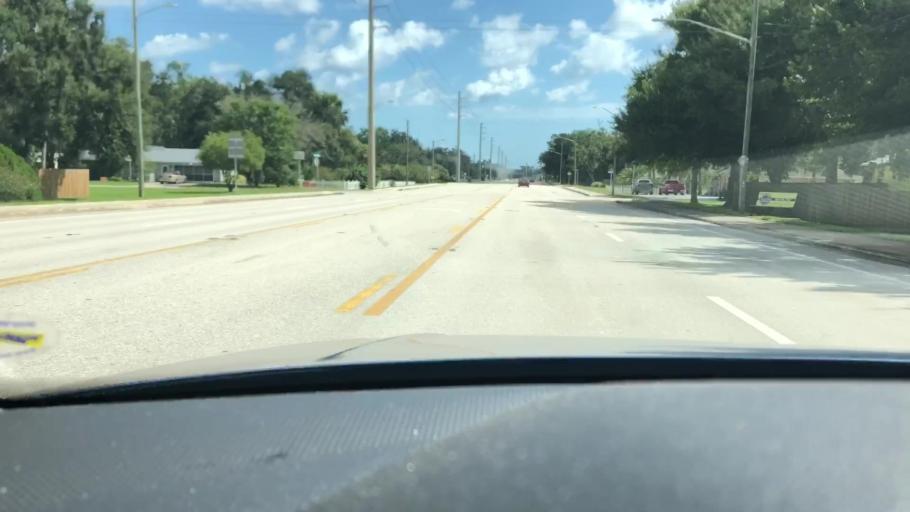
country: US
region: Florida
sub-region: Volusia County
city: Edgewater
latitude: 28.9663
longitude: -80.9122
